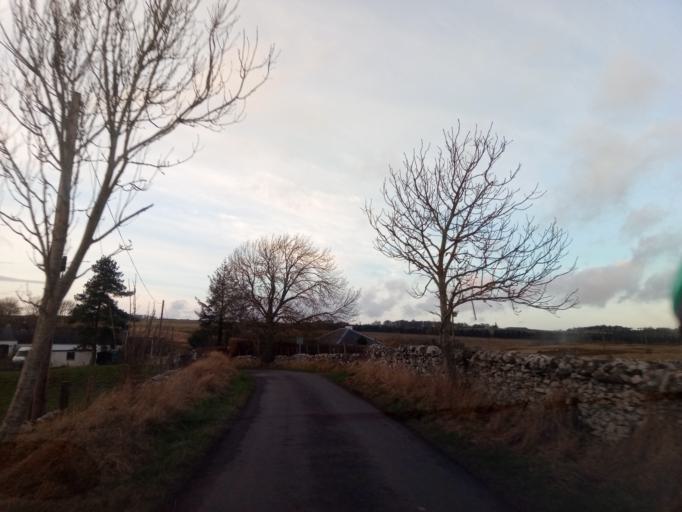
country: GB
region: Scotland
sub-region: The Scottish Borders
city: Newtown St Boswells
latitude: 55.5365
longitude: -2.7150
